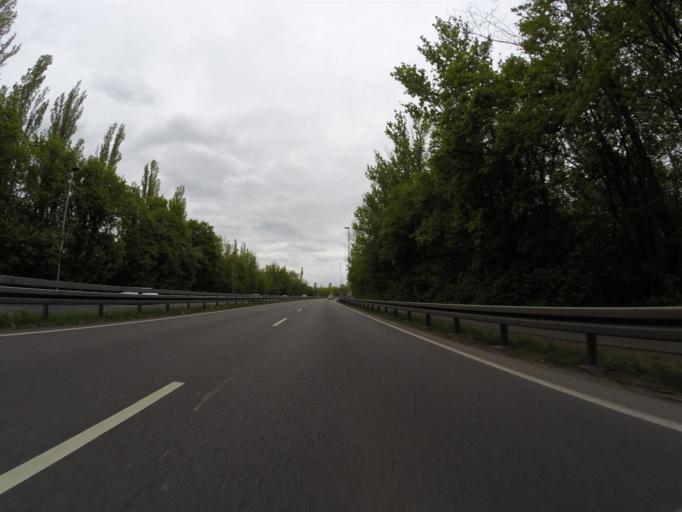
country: DE
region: Saxony-Anhalt
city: Merseburg
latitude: 51.3671
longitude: 11.9803
